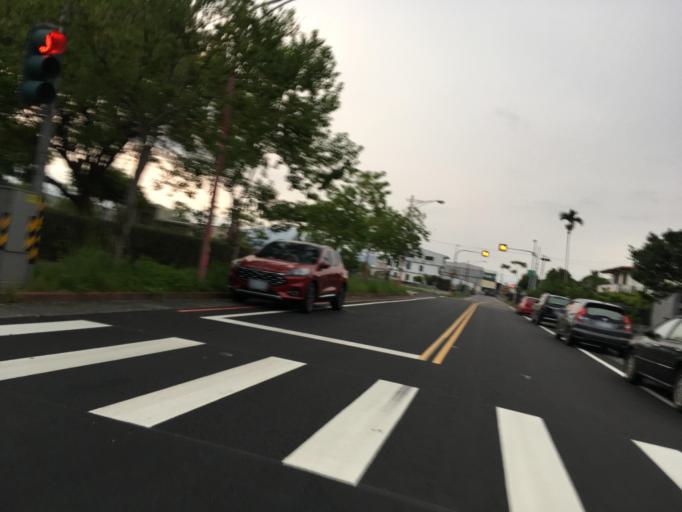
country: TW
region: Taiwan
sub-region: Yilan
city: Yilan
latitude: 24.6647
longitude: 121.7638
